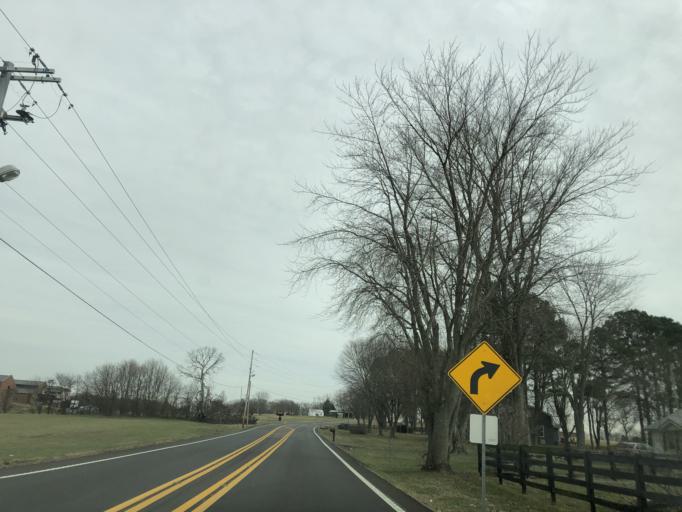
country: US
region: Tennessee
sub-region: Sumner County
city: White House
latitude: 36.4742
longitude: -86.7068
